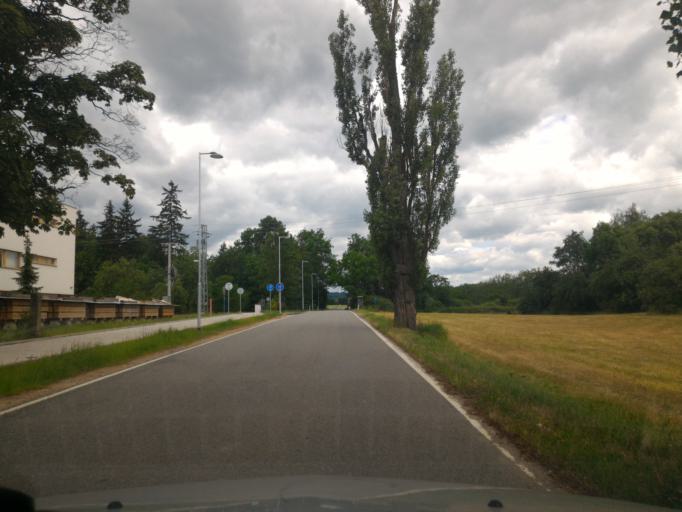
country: CZ
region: Vysocina
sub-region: Okres Jihlava
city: Telc
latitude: 49.1917
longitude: 15.4474
